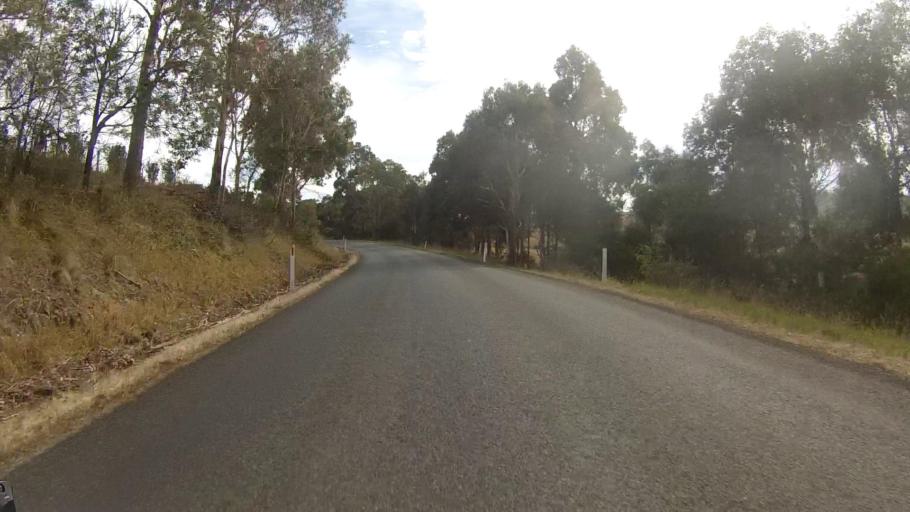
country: AU
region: Tasmania
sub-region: Sorell
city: Sorell
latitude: -42.7882
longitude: 147.8064
